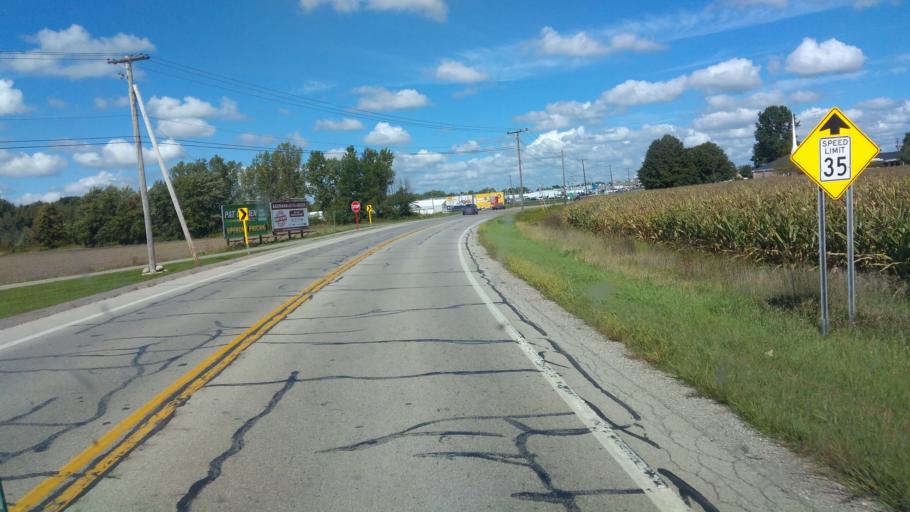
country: US
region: Ohio
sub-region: Huron County
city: Willard
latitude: 41.0338
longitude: -82.7150
